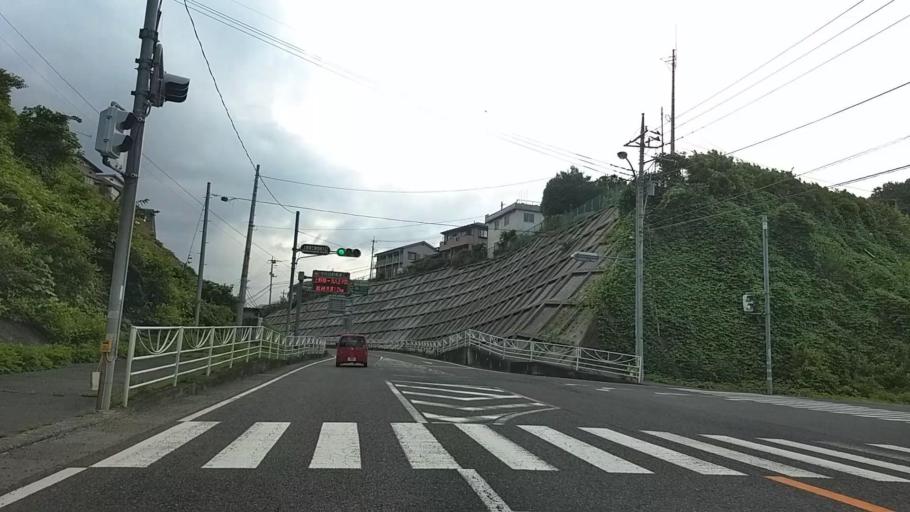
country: JP
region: Yamanashi
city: Uenohara
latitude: 35.6241
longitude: 139.1221
